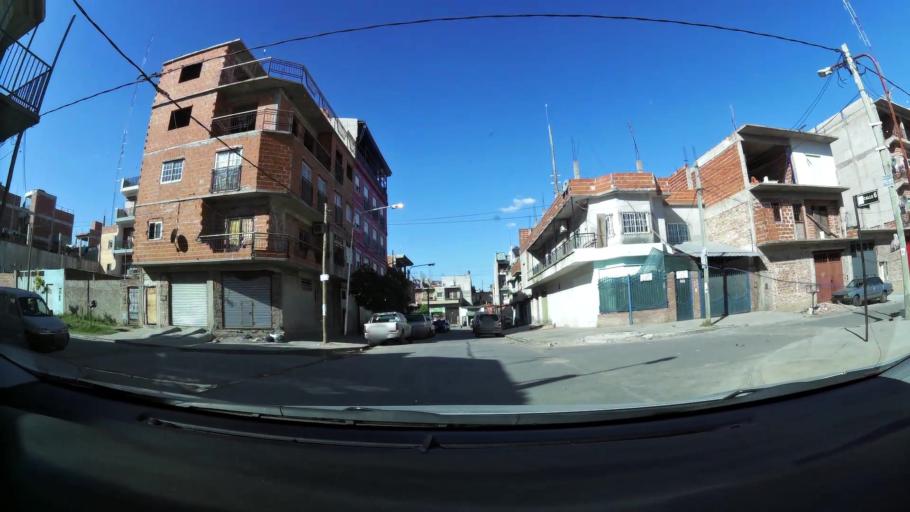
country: AR
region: Buenos Aires F.D.
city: Villa Lugano
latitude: -34.7039
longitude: -58.4818
